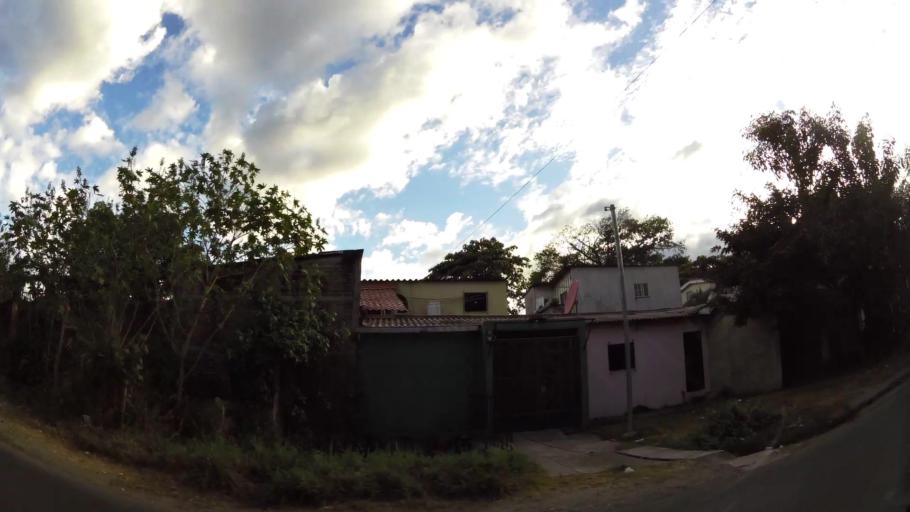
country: SV
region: Cuscatlan
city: Cojutepeque
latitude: 13.7222
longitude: -88.9291
